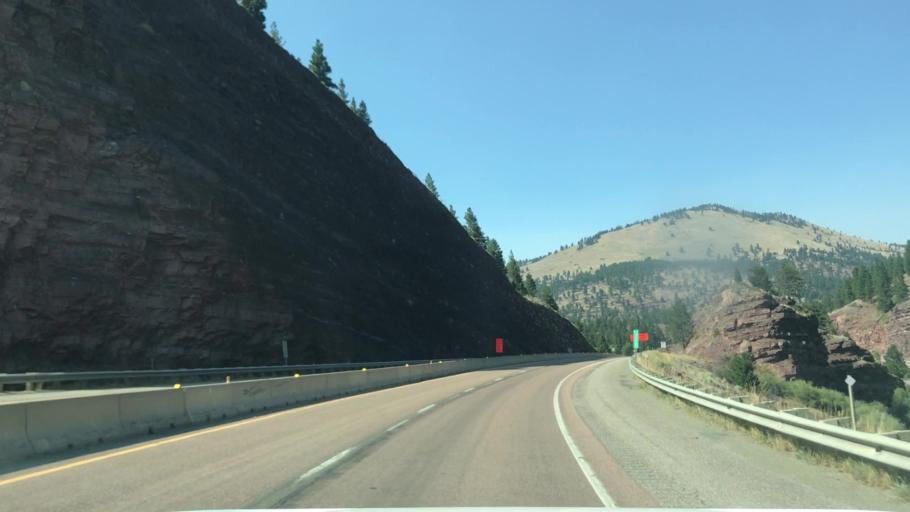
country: US
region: Montana
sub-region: Lewis and Clark County
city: Helena Valley Northwest
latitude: 46.9306
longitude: -112.1257
